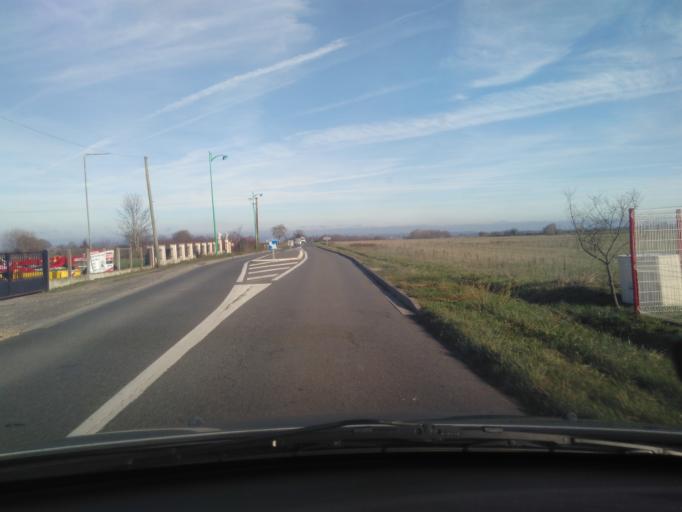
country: FR
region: Centre
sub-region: Departement du Cher
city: Orval
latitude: 46.6579
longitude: 2.4404
